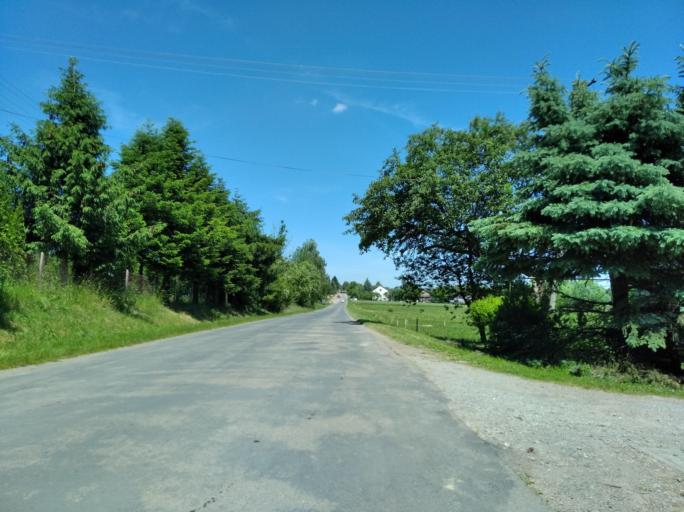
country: PL
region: Subcarpathian Voivodeship
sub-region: Powiat jasielski
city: Tarnowiec
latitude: 49.7059
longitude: 21.5529
